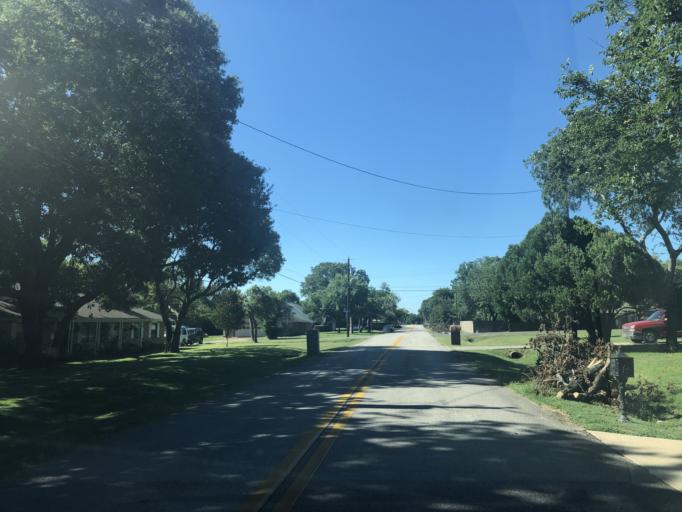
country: US
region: Texas
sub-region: Dallas County
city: Duncanville
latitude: 32.6516
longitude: -96.9356
